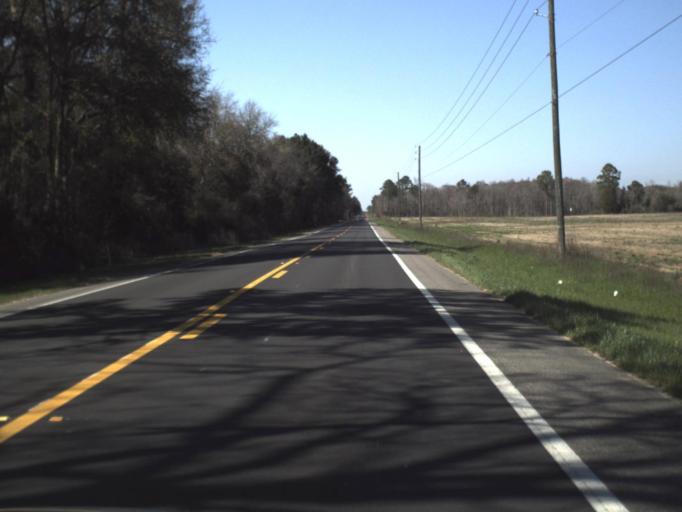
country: US
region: Florida
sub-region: Jackson County
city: Marianna
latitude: 30.6688
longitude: -85.1682
